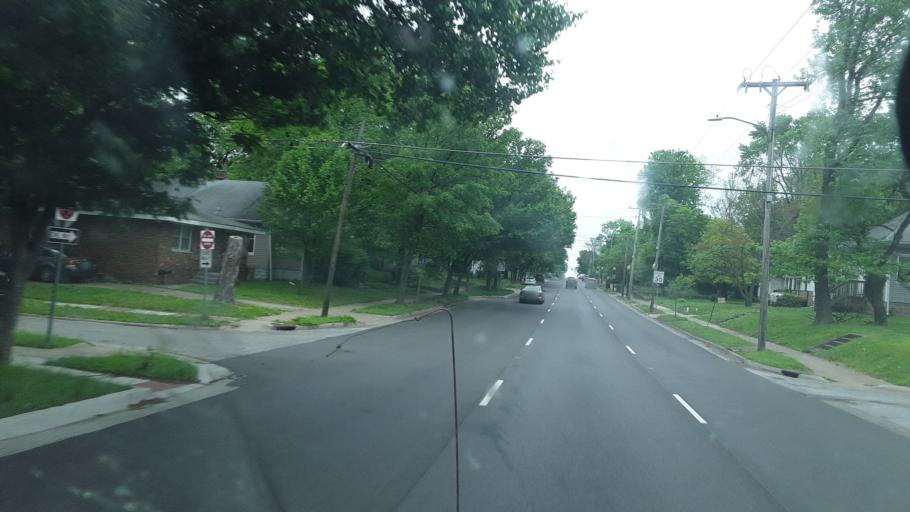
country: US
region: Illinois
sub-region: Jackson County
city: Carbondale
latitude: 37.7245
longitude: -89.2259
